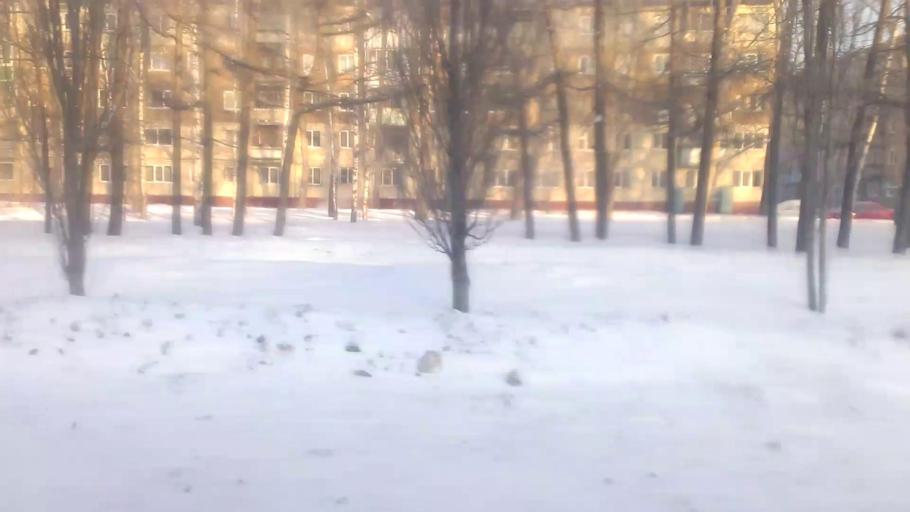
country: RU
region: Altai Krai
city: Novosilikatnyy
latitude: 53.3739
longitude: 83.6677
